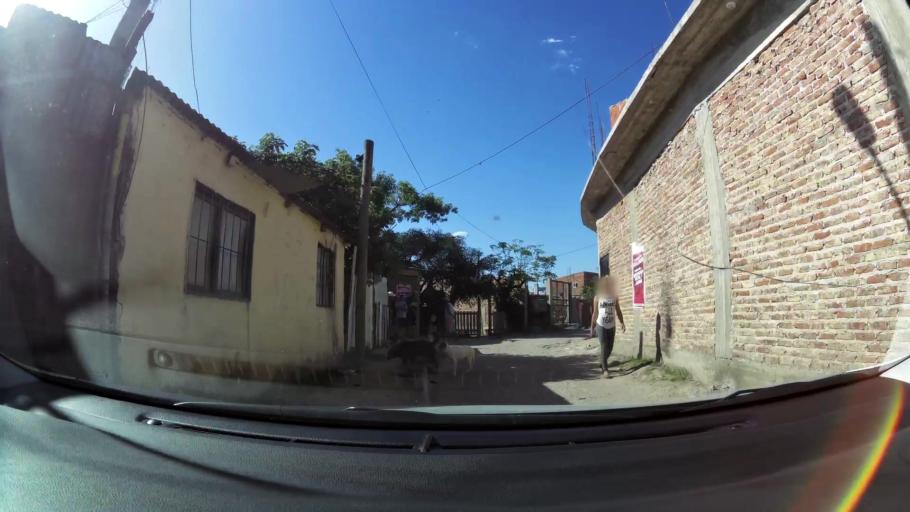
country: AR
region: Buenos Aires F.D.
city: Villa Lugano
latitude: -34.7087
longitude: -58.4870
